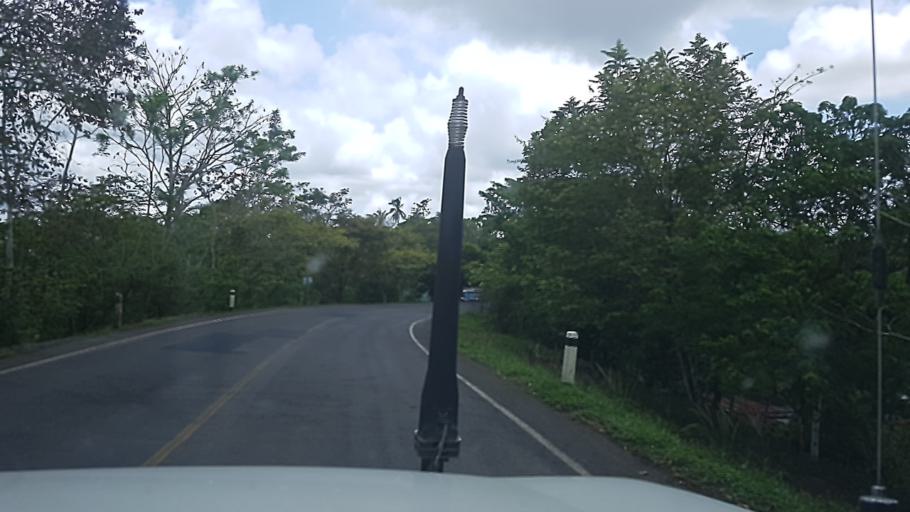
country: NI
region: Atlantico Sur
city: Muelle de los Bueyes
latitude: 11.8864
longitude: -84.6421
